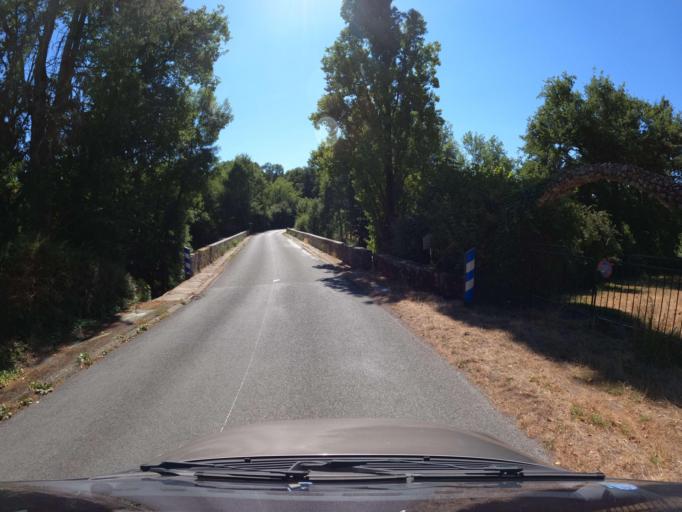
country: FR
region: Pays de la Loire
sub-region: Departement de la Vendee
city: Saint-Aubin-des-Ormeaux
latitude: 47.0030
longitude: -1.0152
